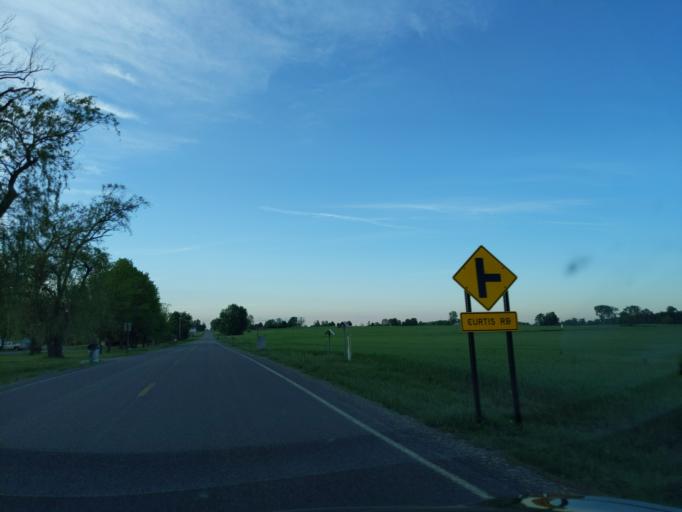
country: US
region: Michigan
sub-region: Ingham County
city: Williamston
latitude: 42.5754
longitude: -84.2985
